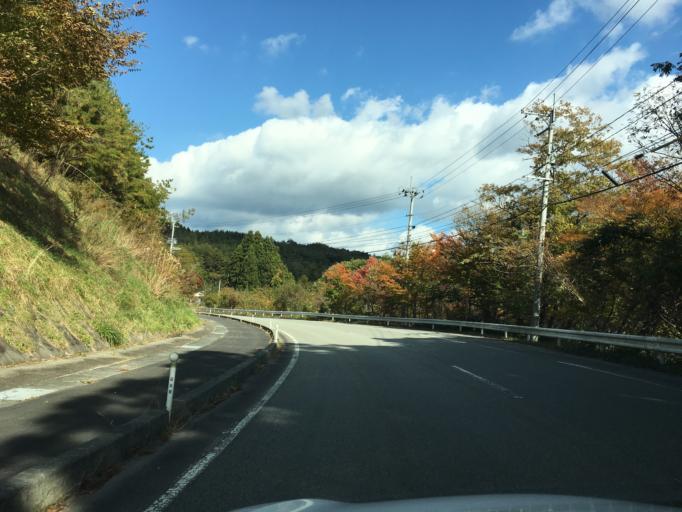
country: JP
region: Fukushima
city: Funehikimachi-funehiki
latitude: 37.3270
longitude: 140.7879
